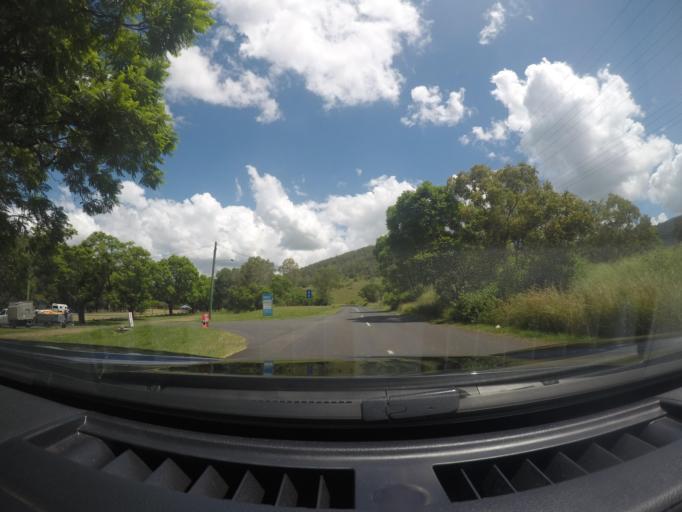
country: AU
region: Queensland
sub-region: Moreton Bay
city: Woodford
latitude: -27.1235
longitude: 152.5506
